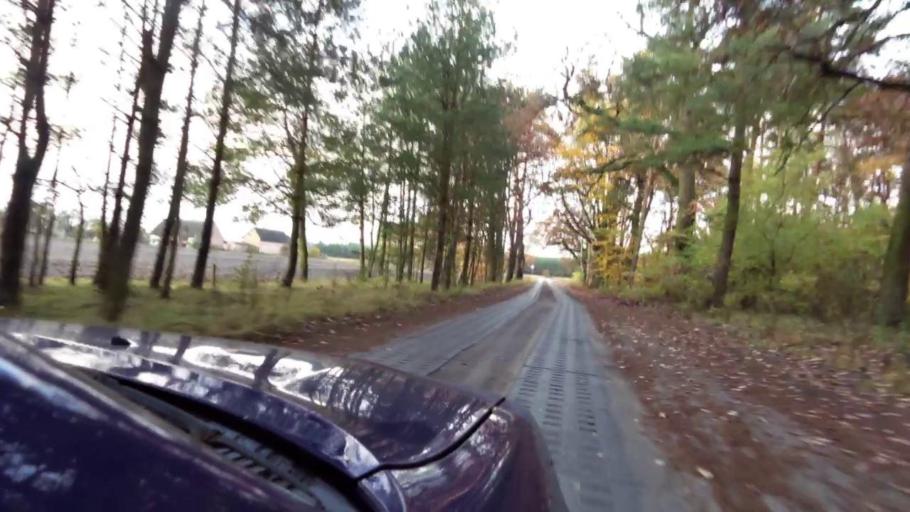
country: PL
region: West Pomeranian Voivodeship
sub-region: Powiat goleniowski
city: Goleniow
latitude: 53.5818
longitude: 14.7653
